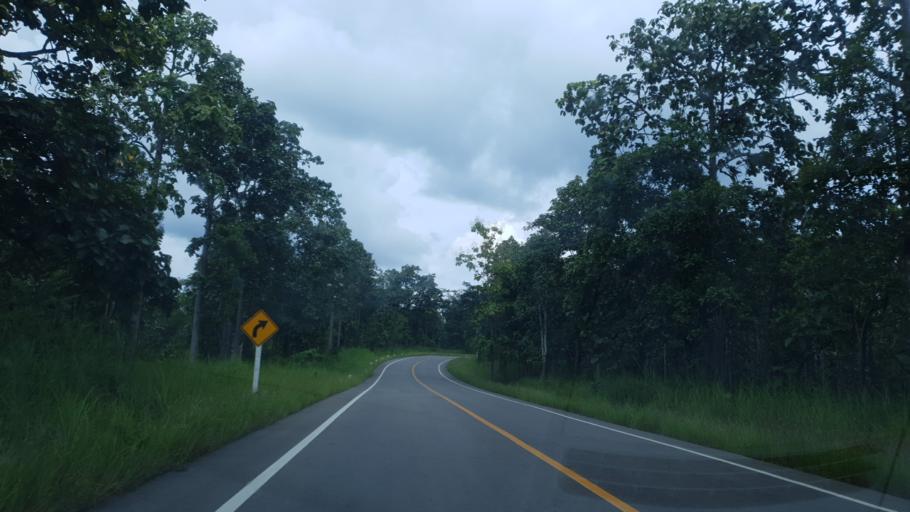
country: TH
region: Mae Hong Son
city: Khun Yuam
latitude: 18.7616
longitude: 97.9324
